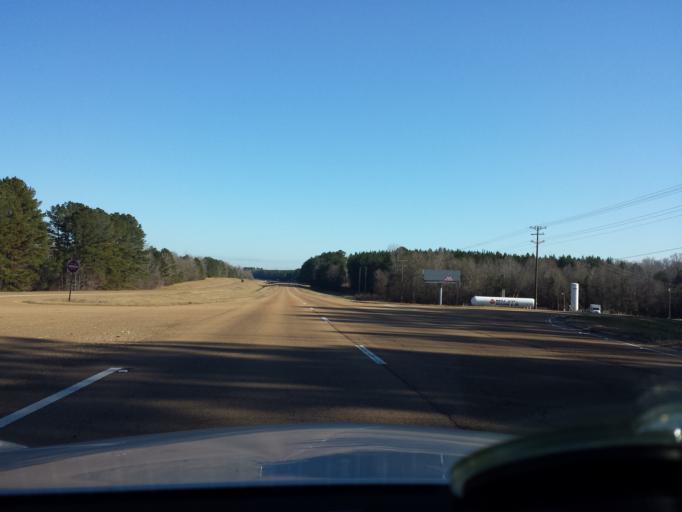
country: US
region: Mississippi
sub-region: Rankin County
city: Brandon
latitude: 32.4328
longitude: -89.9276
